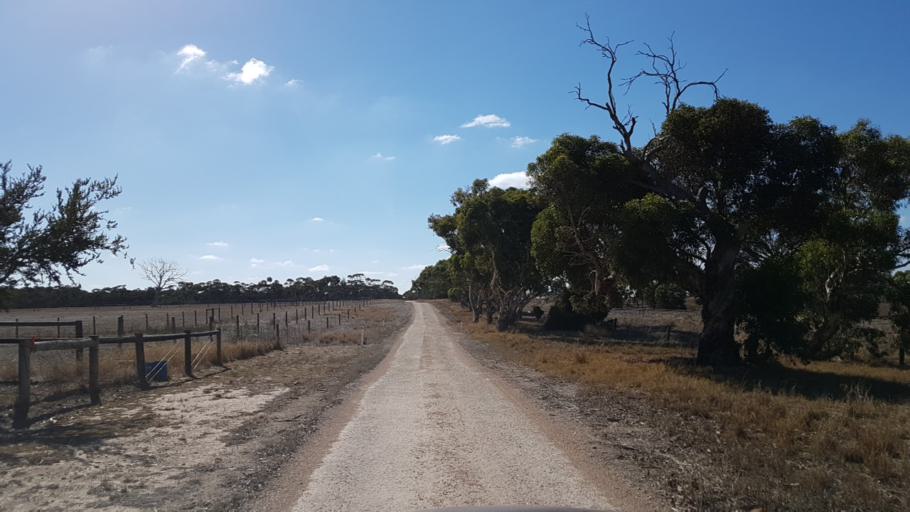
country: AU
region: South Australia
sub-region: Alexandrina
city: Goolwa
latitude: -35.3810
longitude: 138.8271
